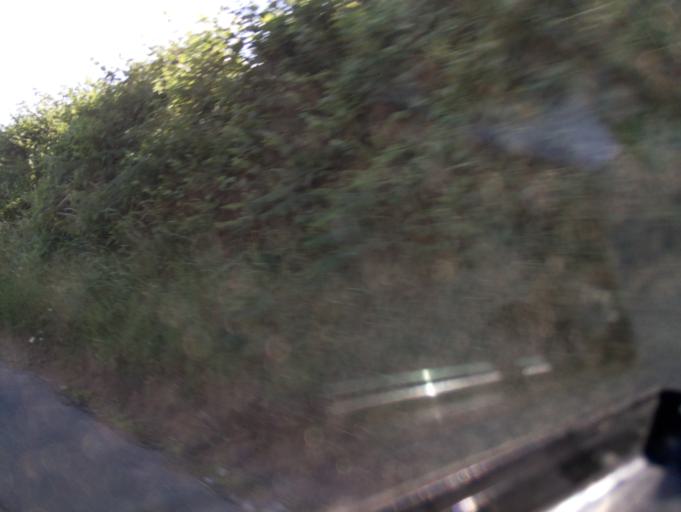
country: GB
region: England
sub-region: Herefordshire
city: Yatton
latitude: 51.9668
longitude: -2.5514
